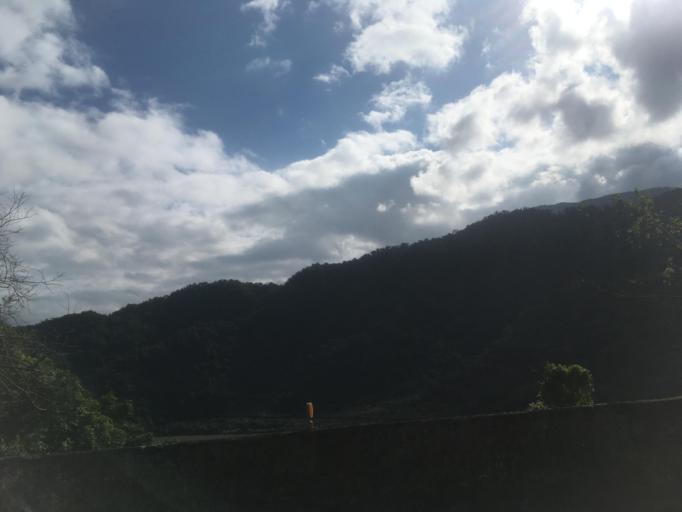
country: TW
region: Taiwan
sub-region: Yilan
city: Yilan
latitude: 24.6294
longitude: 121.5453
